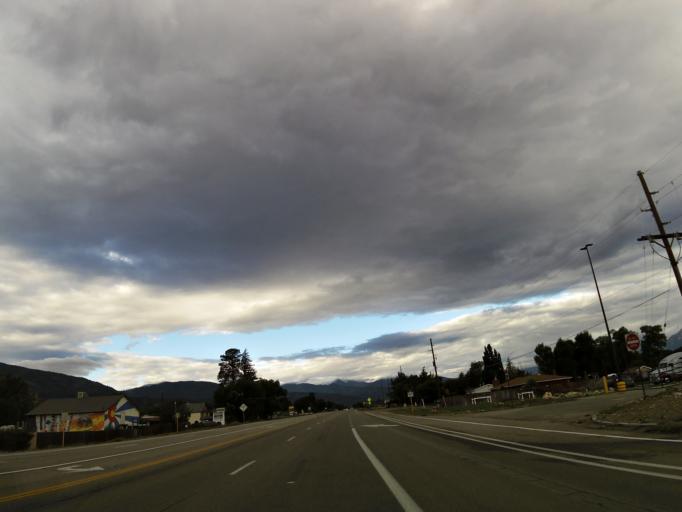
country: US
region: Colorado
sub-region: Chaffee County
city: Salida
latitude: 38.5230
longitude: -106.0225
